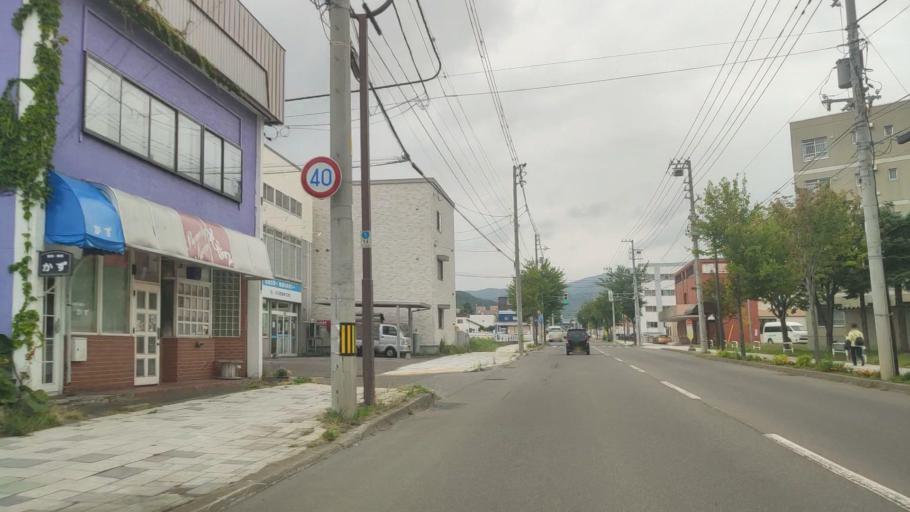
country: JP
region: Hokkaido
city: Otaru
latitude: 43.1723
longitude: 141.0547
